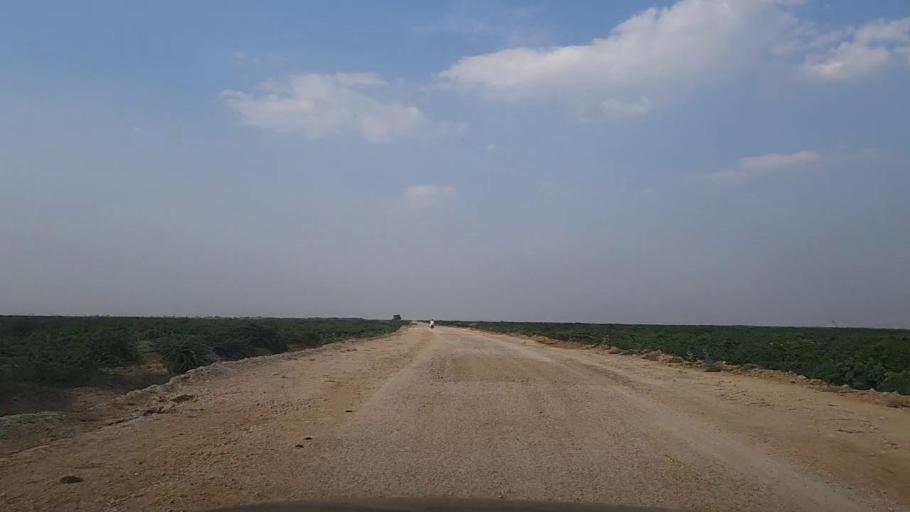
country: PK
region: Sindh
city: Gharo
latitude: 24.8234
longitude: 67.7449
